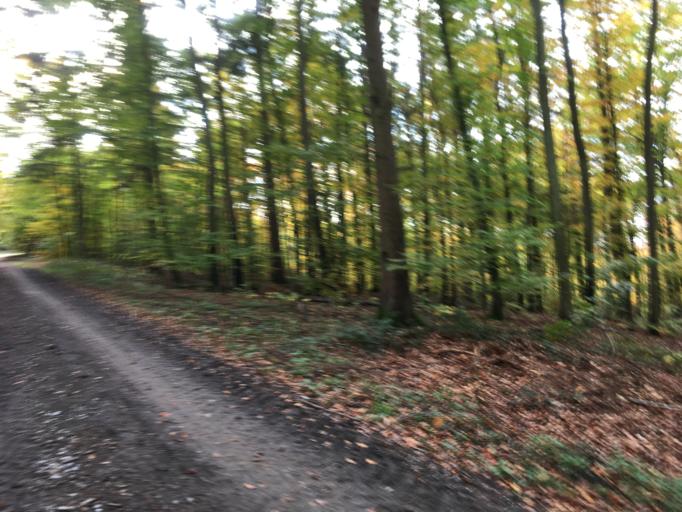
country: DE
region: Baden-Wuerttemberg
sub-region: Karlsruhe Region
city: Waibstadt
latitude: 49.2767
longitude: 8.9401
